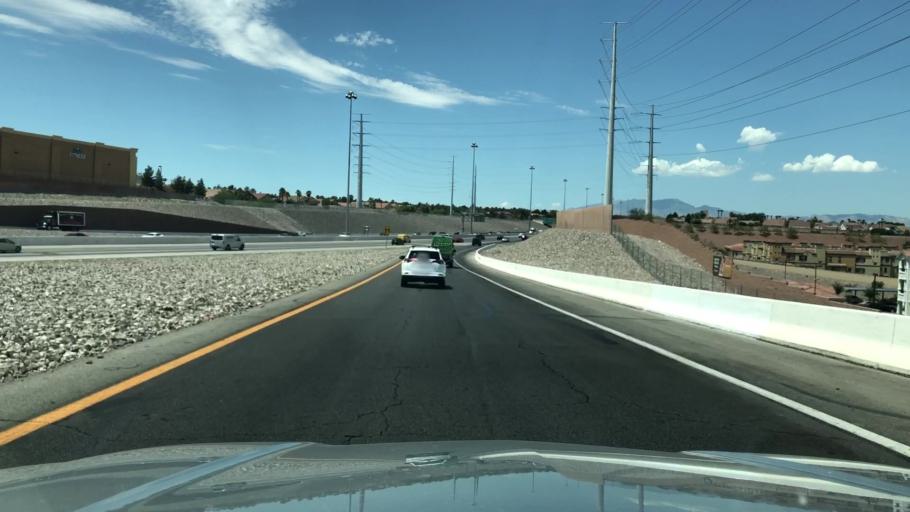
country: US
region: Nevada
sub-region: Clark County
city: Whitney
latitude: 36.0298
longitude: -115.0490
